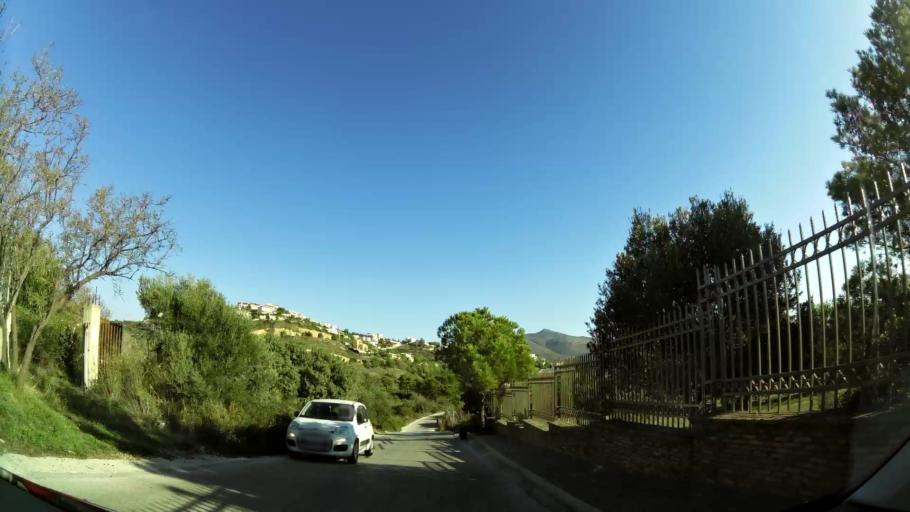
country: GR
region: Attica
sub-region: Nomarchia Anatolikis Attikis
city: Dhrafi
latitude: 38.0171
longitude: 23.9026
